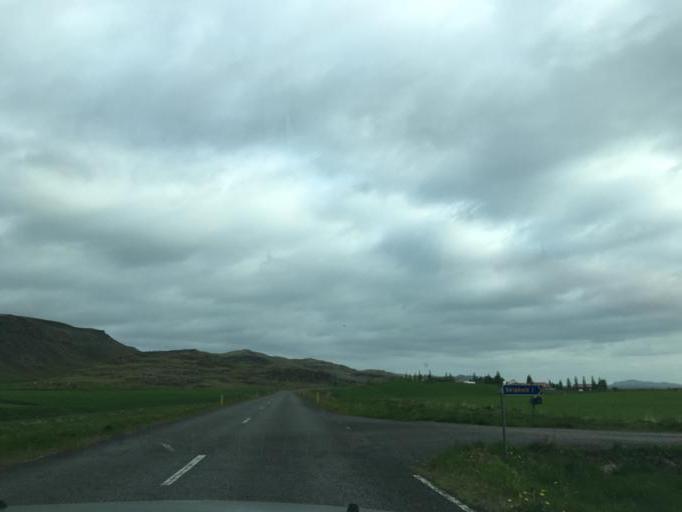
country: IS
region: South
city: Vestmannaeyjar
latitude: 64.1929
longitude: -20.2778
